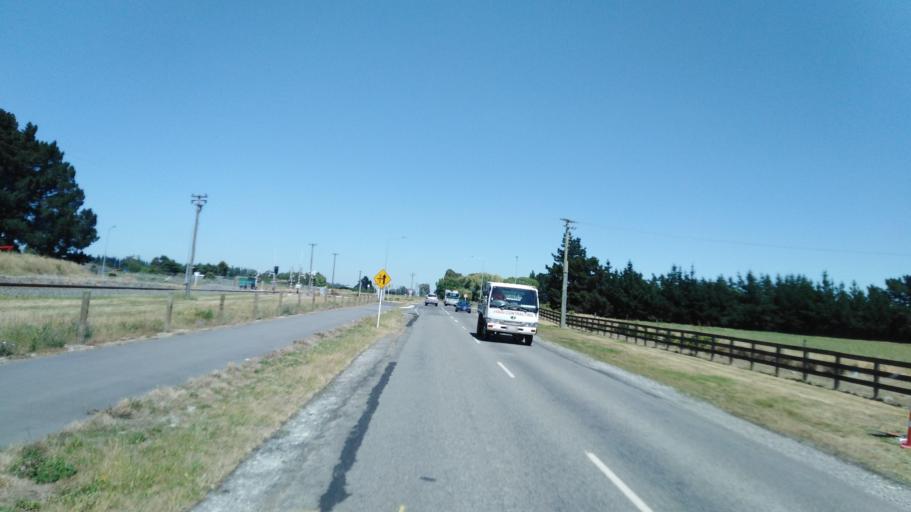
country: NZ
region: Canterbury
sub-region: Selwyn District
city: Rolleston
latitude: -43.5653
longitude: 172.4445
